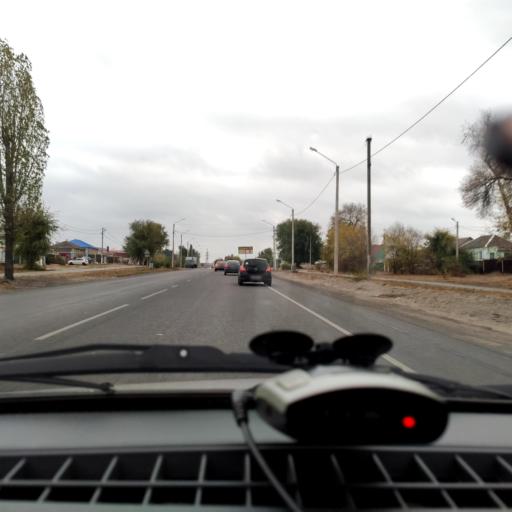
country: RU
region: Voronezj
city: Pridonskoy
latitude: 51.7052
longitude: 39.0755
